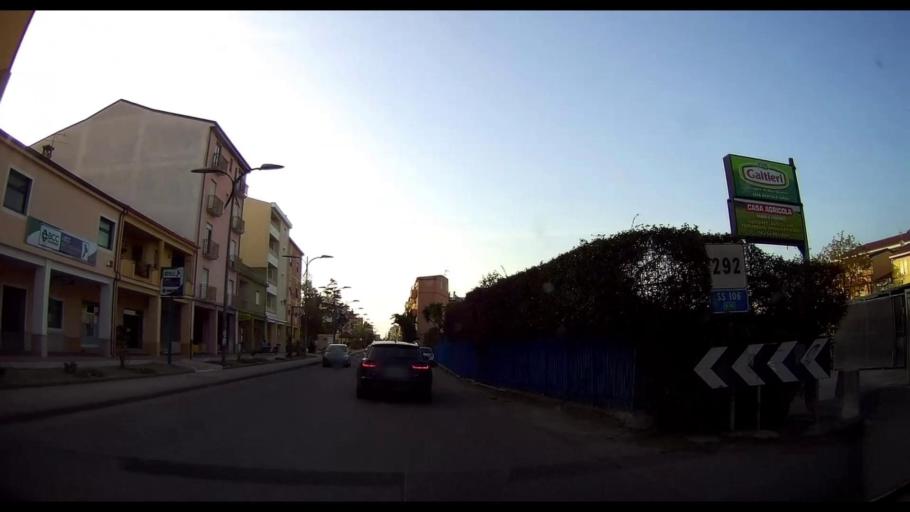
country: IT
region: Calabria
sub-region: Provincia di Crotone
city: Torretta
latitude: 39.4495
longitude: 17.0403
